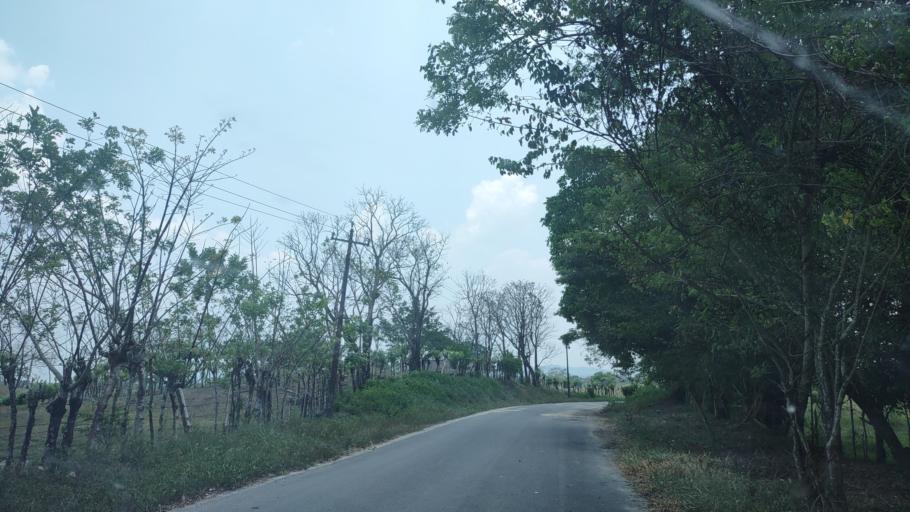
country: MX
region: Tabasco
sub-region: Huimanguillo
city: Francisco Rueda
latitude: 17.6095
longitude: -94.0925
